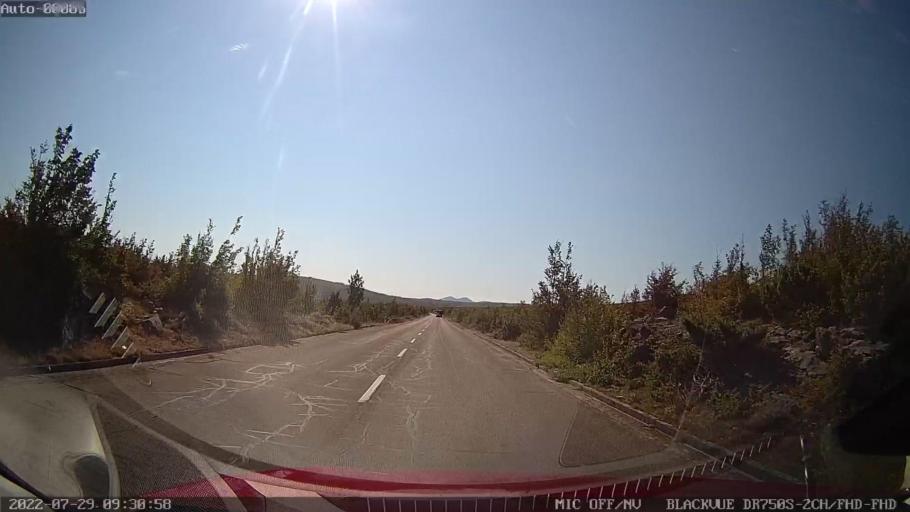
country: HR
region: Zadarska
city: Obrovac
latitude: 44.1918
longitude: 15.6930
